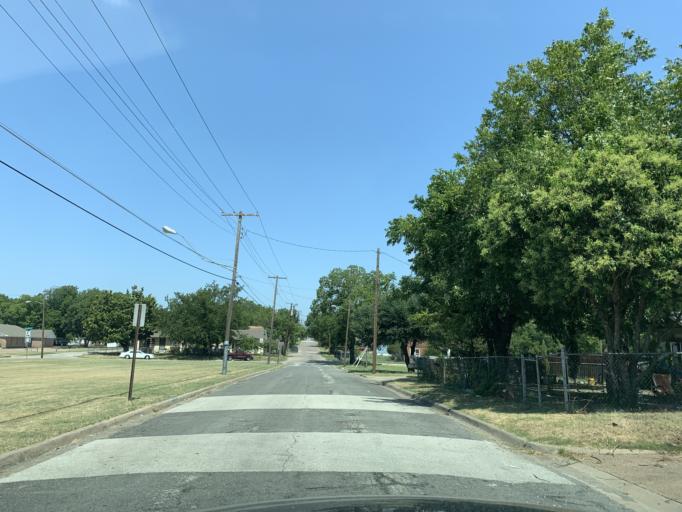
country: US
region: Texas
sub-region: Dallas County
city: Hutchins
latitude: 32.6853
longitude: -96.7960
